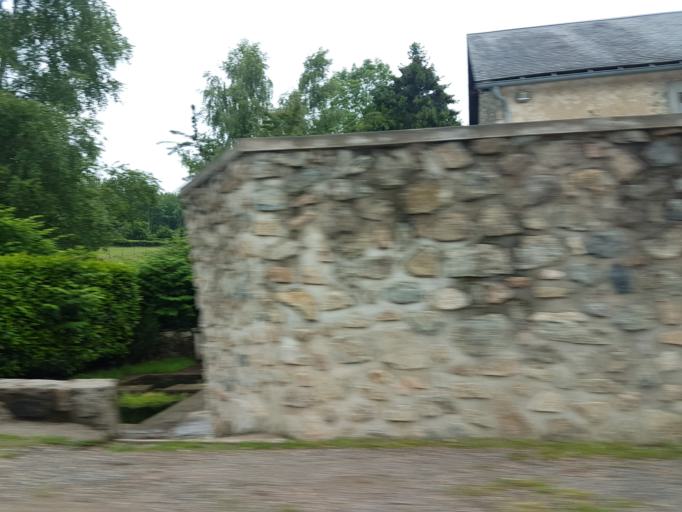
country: FR
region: Bourgogne
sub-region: Departement de la Nievre
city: Chateau-Chinon(Ville)
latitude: 47.0409
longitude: 4.0002
